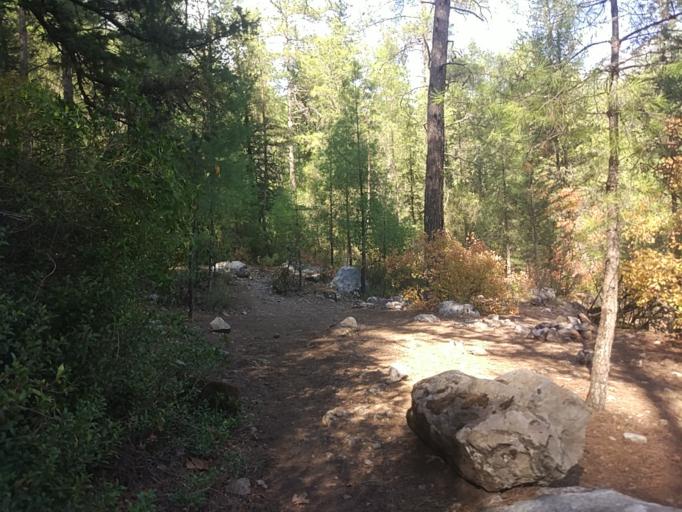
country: TR
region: Antalya
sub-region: Kemer
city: Goeynuek
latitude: 36.6760
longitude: 30.4947
